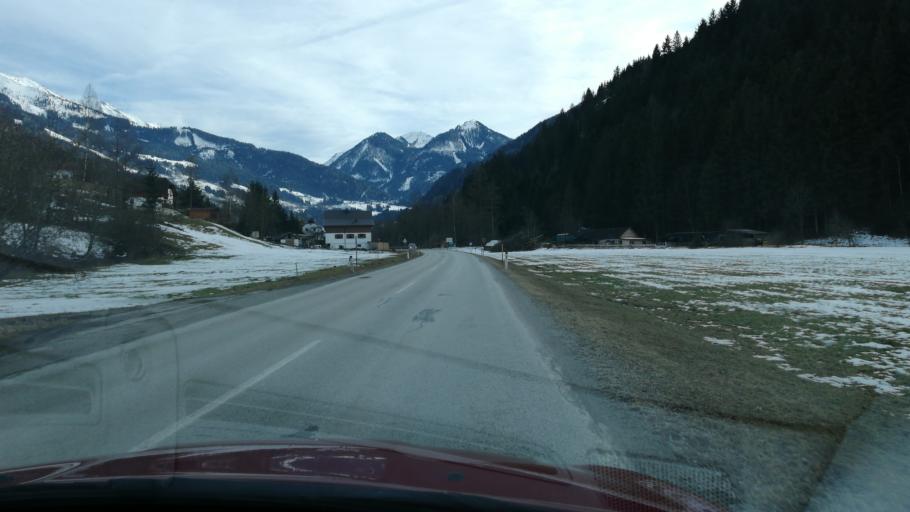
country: AT
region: Styria
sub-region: Politischer Bezirk Liezen
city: Donnersbach
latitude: 47.4767
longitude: 14.1183
